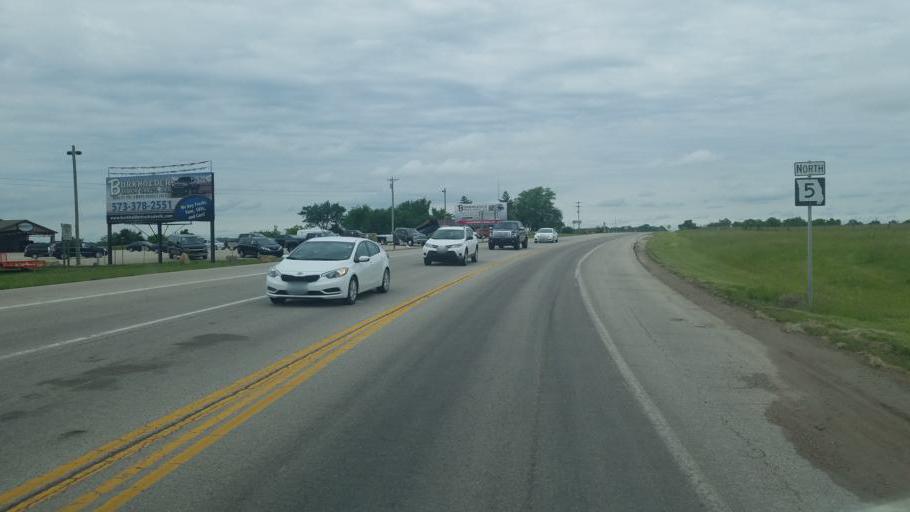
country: US
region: Missouri
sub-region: Morgan County
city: Versailles
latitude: 38.4475
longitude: -92.8092
